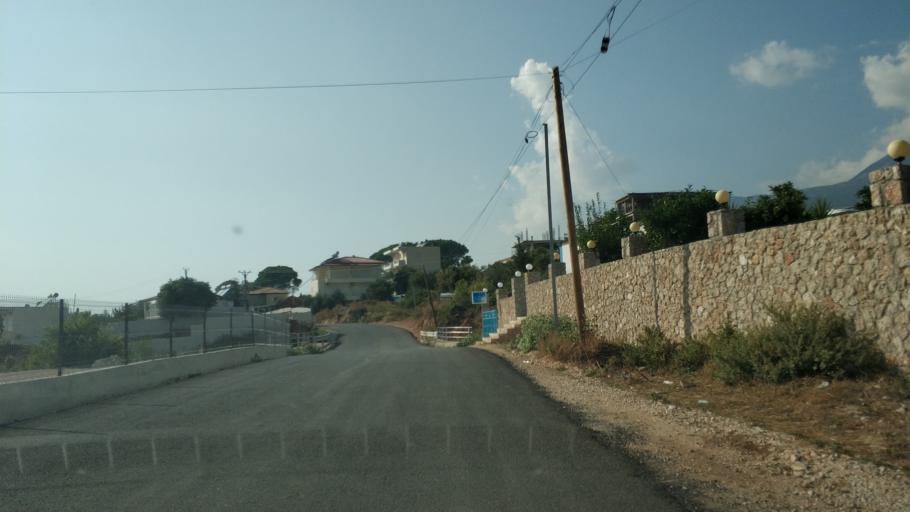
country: AL
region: Vlore
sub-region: Rrethi i Vlores
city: Vranisht
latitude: 40.1448
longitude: 19.6364
